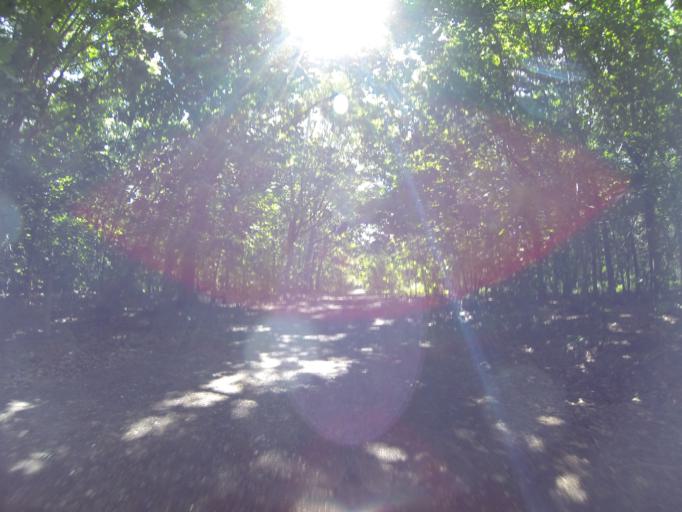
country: GB
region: England
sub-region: Greater London
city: Bexley
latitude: 51.4249
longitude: 0.1560
